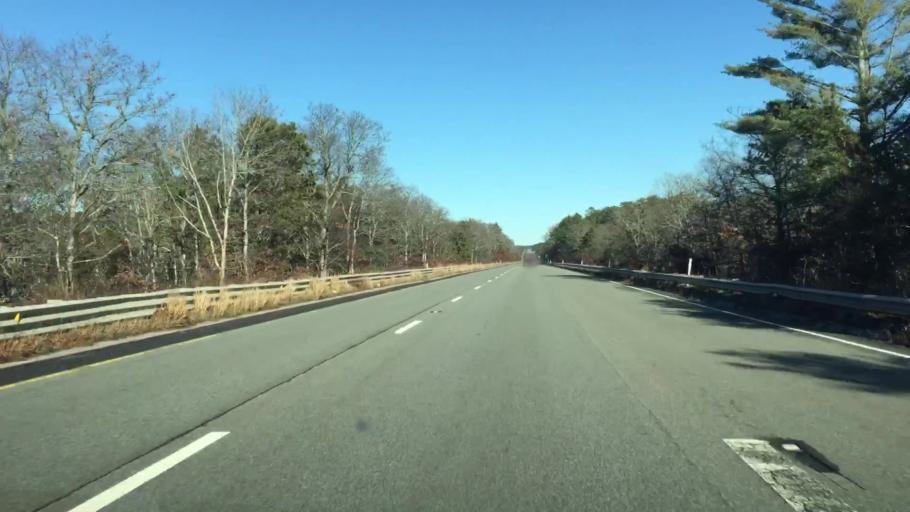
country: US
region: Massachusetts
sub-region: Barnstable County
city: West Falmouth
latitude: 41.6197
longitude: -70.6181
